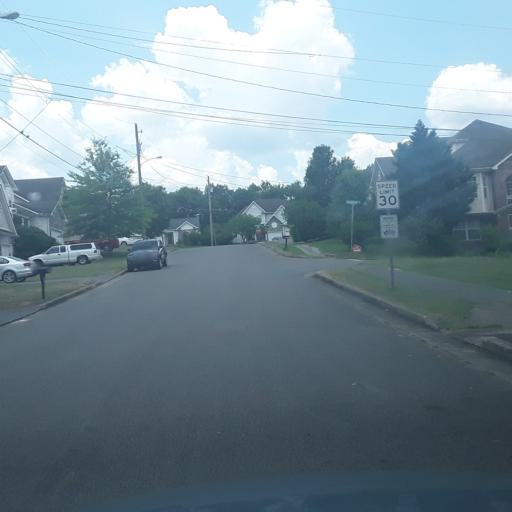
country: US
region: Tennessee
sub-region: Williamson County
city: Brentwood Estates
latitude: 36.0406
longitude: -86.6998
